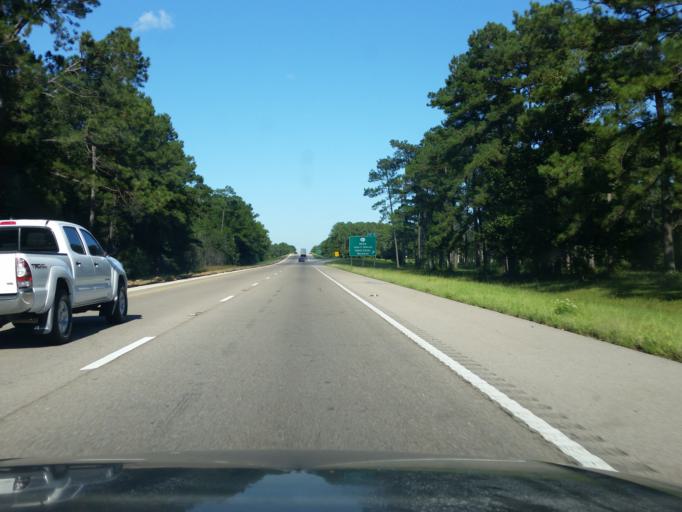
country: US
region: Mississippi
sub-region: Hancock County
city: Pearlington
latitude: 30.3137
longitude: -89.6036
